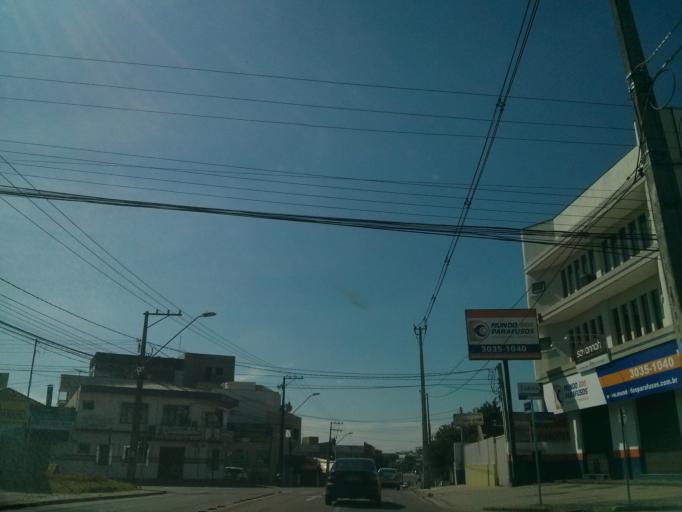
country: BR
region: Parana
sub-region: Sao Jose Dos Pinhais
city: Sao Jose dos Pinhais
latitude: -25.5480
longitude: -49.1974
